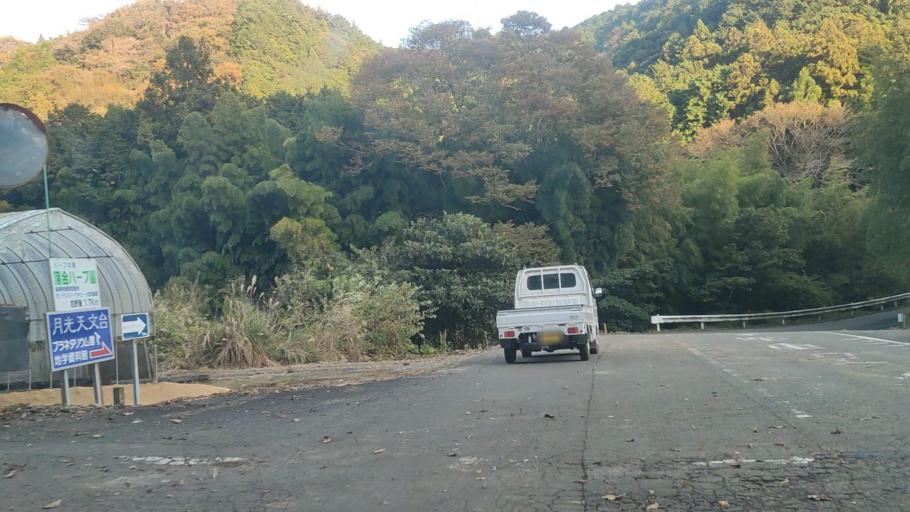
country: JP
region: Shizuoka
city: Mishima
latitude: 35.1345
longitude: 138.9821
